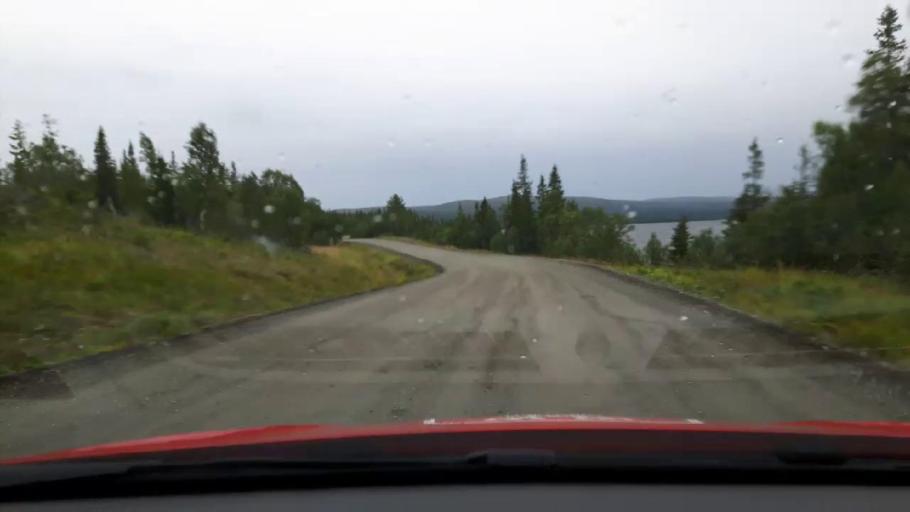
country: NO
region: Nord-Trondelag
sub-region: Meraker
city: Meraker
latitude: 63.5578
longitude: 12.3703
